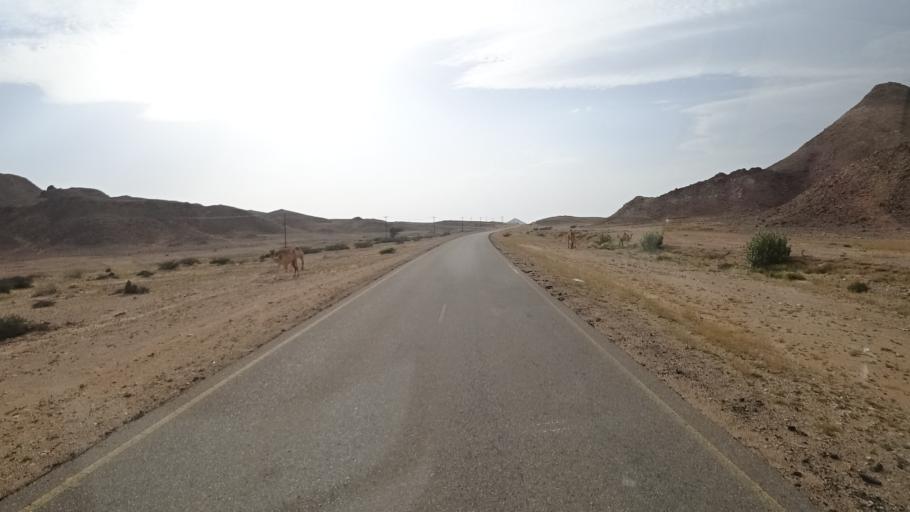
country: OM
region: Ash Sharqiyah
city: Sur
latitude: 22.4348
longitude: 59.8105
